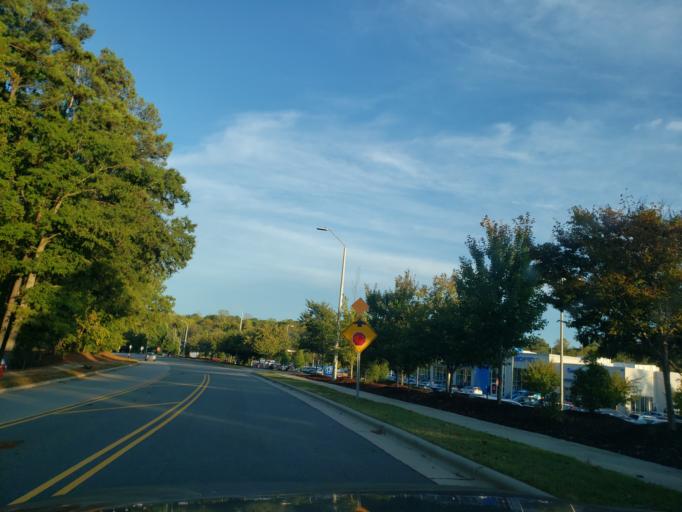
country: US
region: North Carolina
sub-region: Wake County
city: Apex
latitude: 35.7389
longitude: -78.8120
